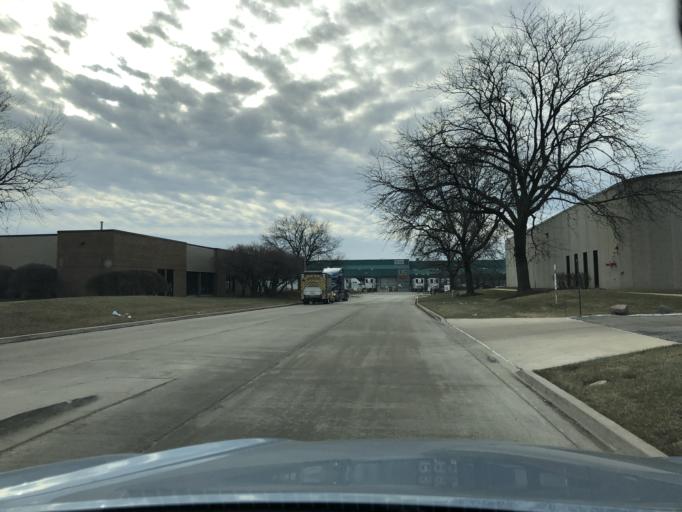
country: US
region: Illinois
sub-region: DuPage County
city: Bensenville
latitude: 41.9804
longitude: -87.9527
